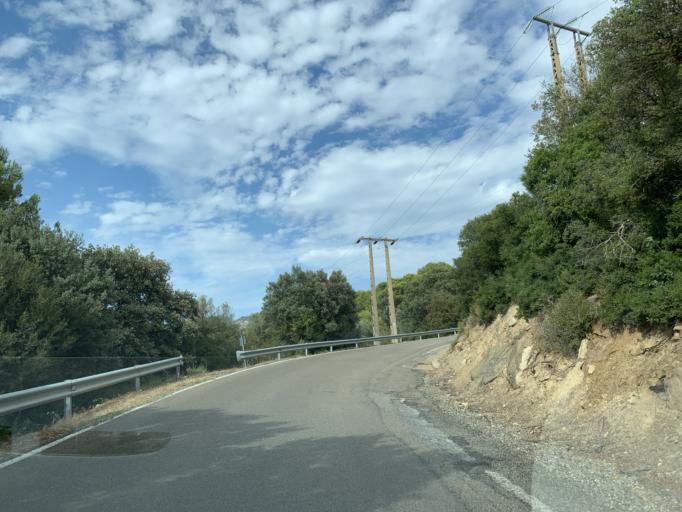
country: ES
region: Aragon
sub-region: Provincia de Zaragoza
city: Santa Eulalia de Gallego
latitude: 42.3157
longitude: -0.7475
